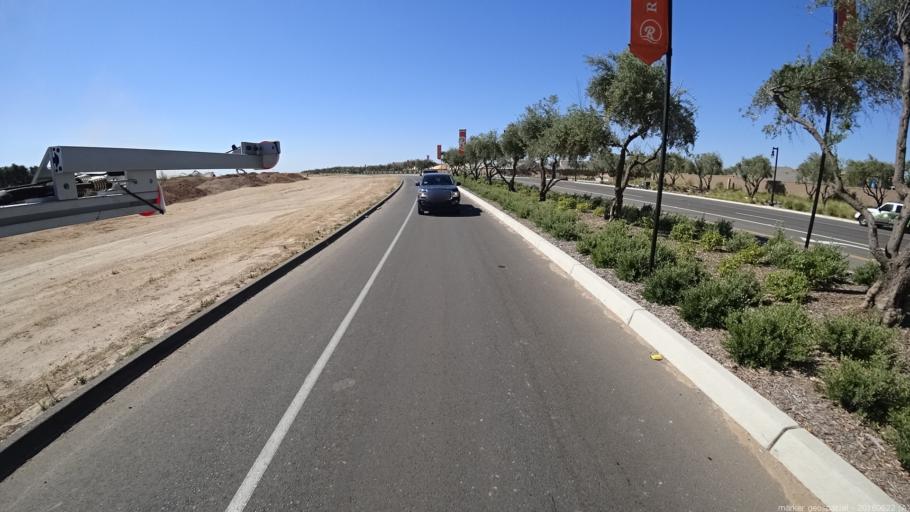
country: US
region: California
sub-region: Madera County
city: Bonadelle Ranchos-Madera Ranchos
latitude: 36.9212
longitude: -119.7991
